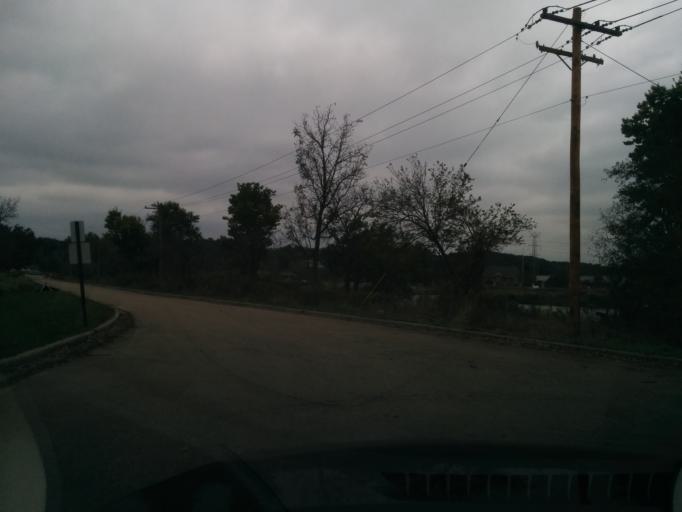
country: US
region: Illinois
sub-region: DuPage County
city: Burr Ridge
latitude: 41.6935
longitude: -87.9330
